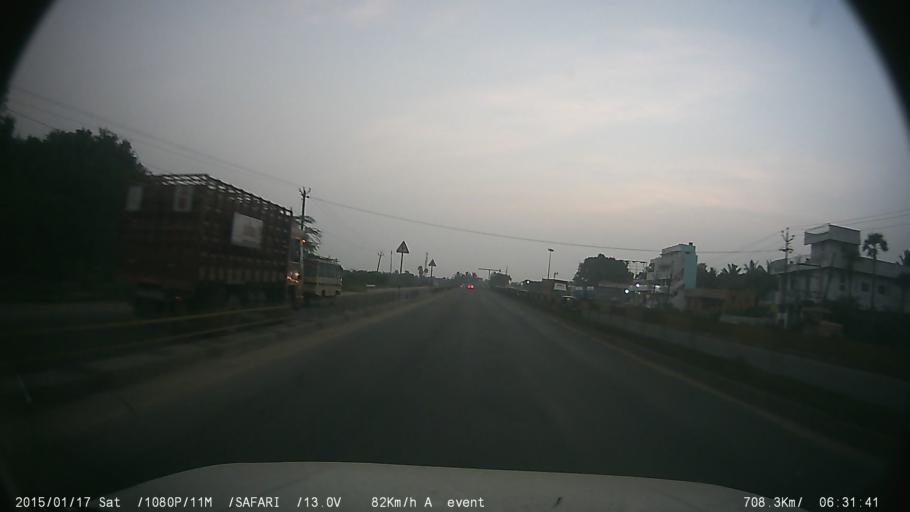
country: IN
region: Tamil Nadu
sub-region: Kancheepuram
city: Sriperumbudur
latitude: 12.9554
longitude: 79.9392
